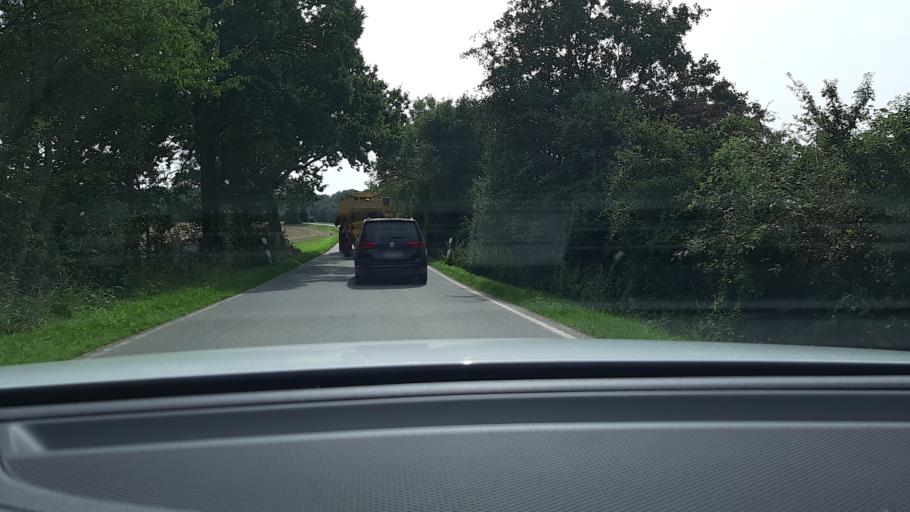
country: DE
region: Schleswig-Holstein
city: Rehhorst
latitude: 53.8627
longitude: 10.4650
